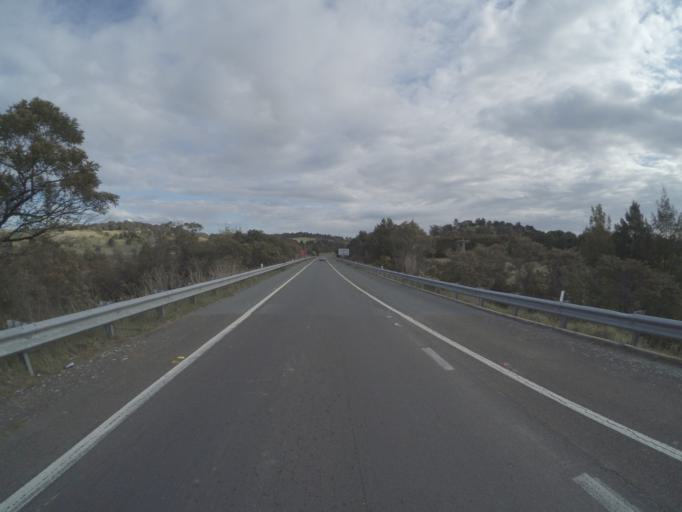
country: AU
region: New South Wales
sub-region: Wingecarribee
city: Bundanoon
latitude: -34.5864
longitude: 150.2489
